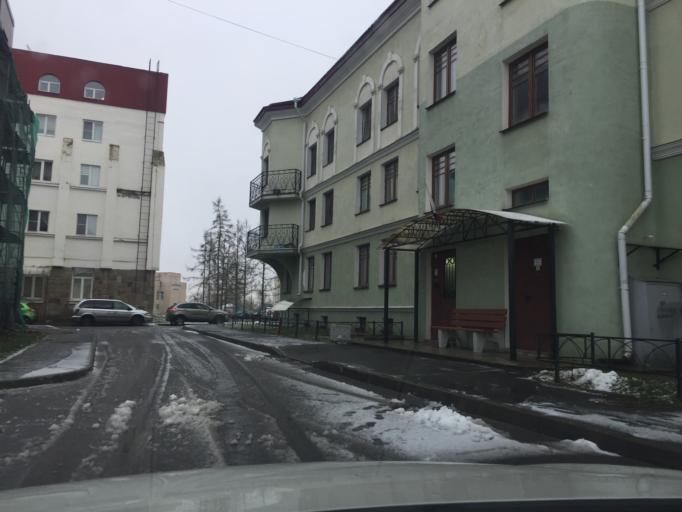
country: RU
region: St.-Petersburg
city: Pushkin
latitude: 59.7038
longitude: 30.3936
